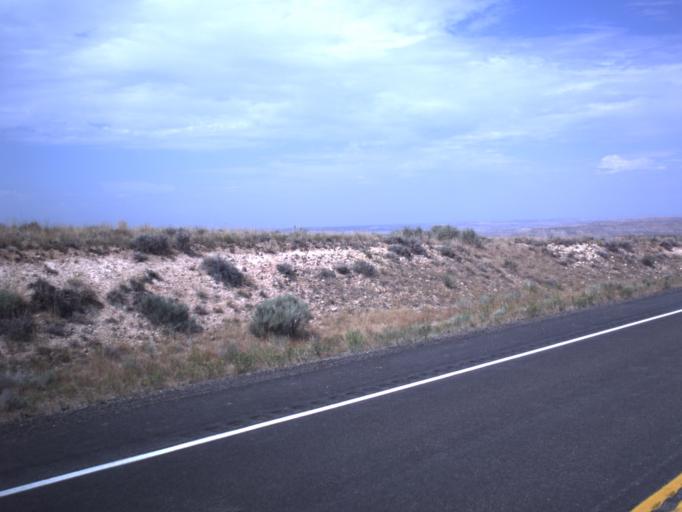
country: US
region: Utah
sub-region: Uintah County
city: Naples
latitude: 40.2734
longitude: -109.4619
